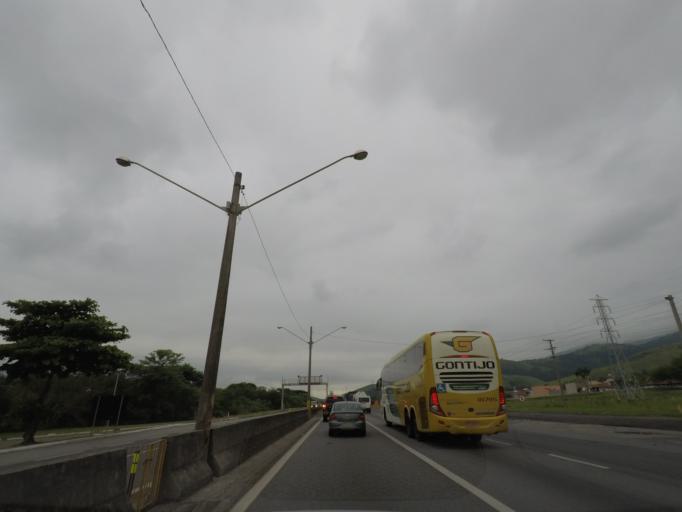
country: BR
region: Sao Paulo
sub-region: Aparecida
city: Aparecida
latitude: -22.8919
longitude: -45.2913
